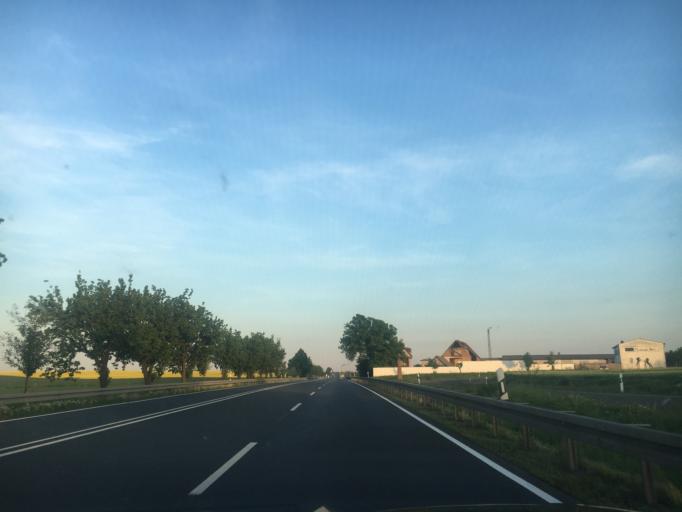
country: DE
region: Saxony-Anhalt
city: Nessa
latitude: 51.1492
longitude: 12.0350
